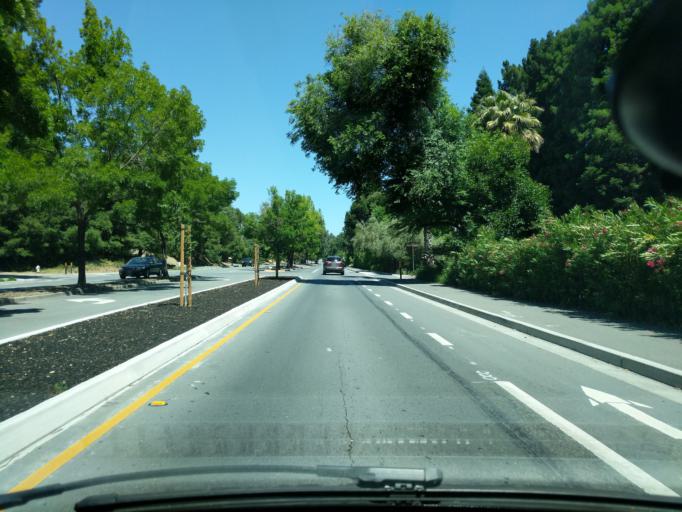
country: US
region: California
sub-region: Contra Costa County
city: Saranap
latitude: 37.8887
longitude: -122.0931
